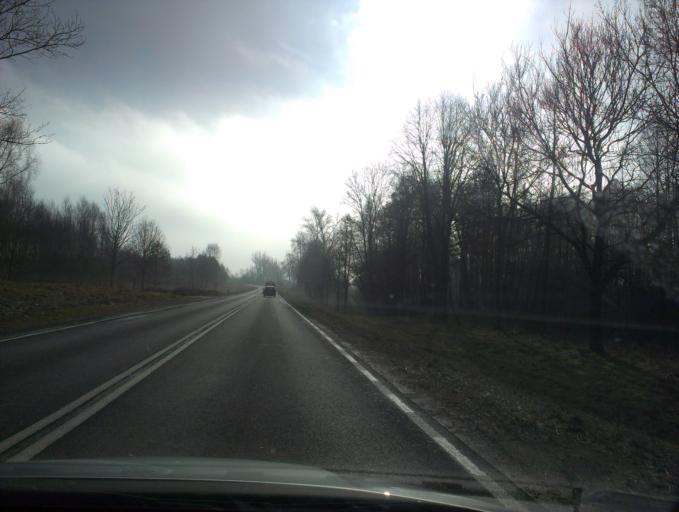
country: PL
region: West Pomeranian Voivodeship
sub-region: Powiat koszalinski
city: Bobolice
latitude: 53.9703
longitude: 16.5600
